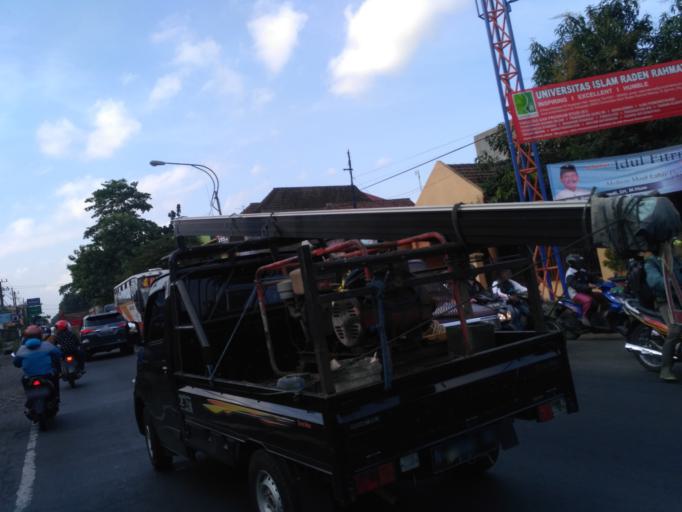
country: ID
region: East Java
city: Pakisaji
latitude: -8.0633
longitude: 112.6001
